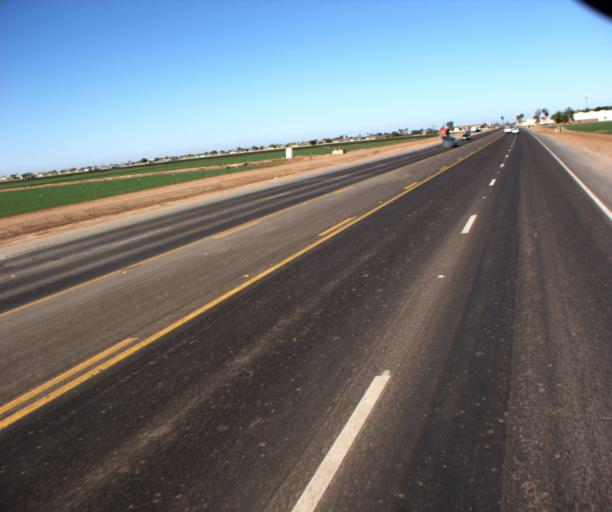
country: US
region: Arizona
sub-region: Yuma County
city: Somerton
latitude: 32.5968
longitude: -114.6936
